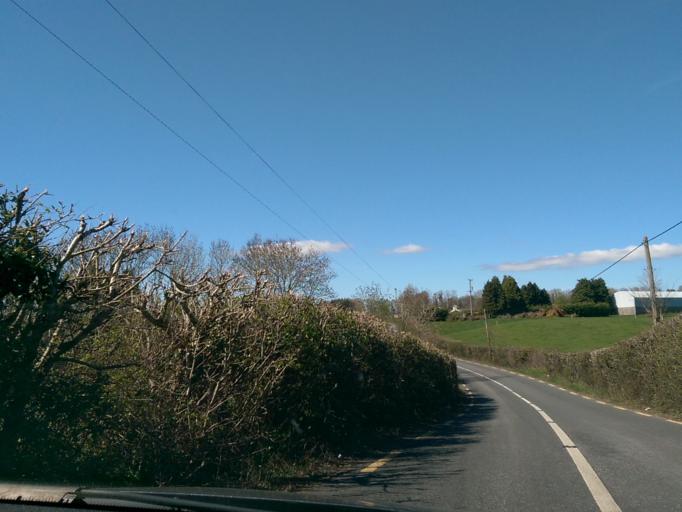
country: IE
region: Leinster
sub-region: Kildare
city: Moone
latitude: 52.9905
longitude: -6.7904
